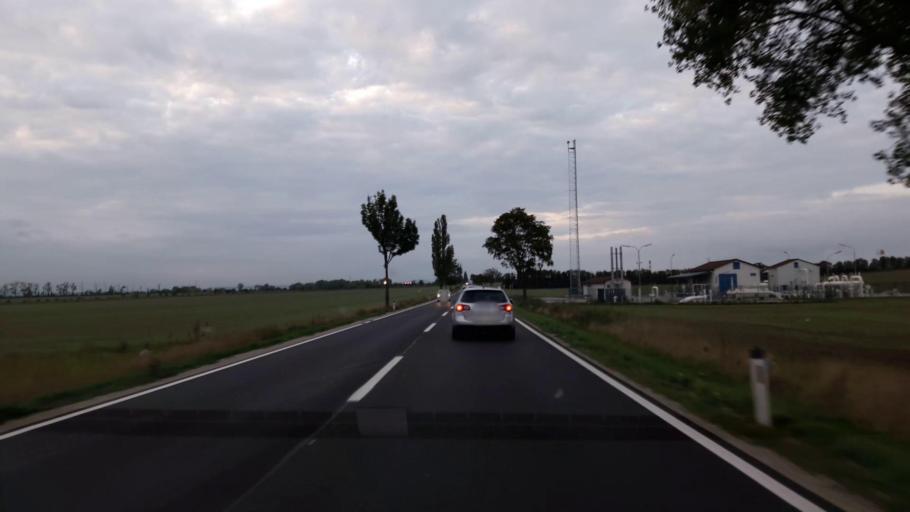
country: AT
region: Lower Austria
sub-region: Politischer Bezirk Wien-Umgebung
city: Rauchenwarth
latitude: 48.1221
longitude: 16.5101
